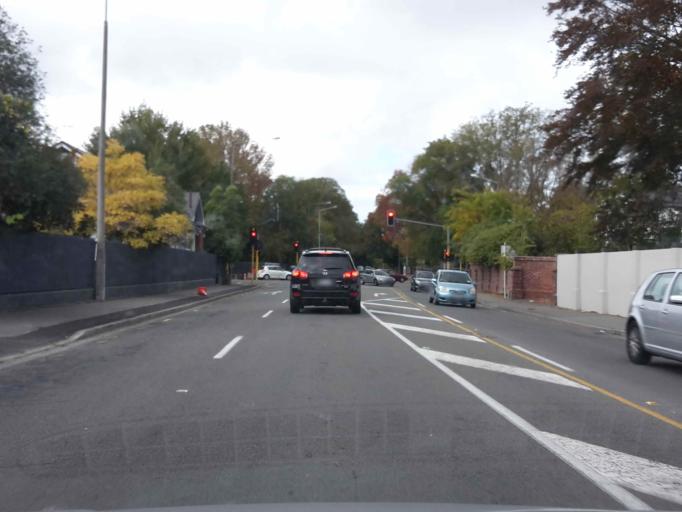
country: NZ
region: Canterbury
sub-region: Christchurch City
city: Christchurch
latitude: -43.5135
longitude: 172.6082
